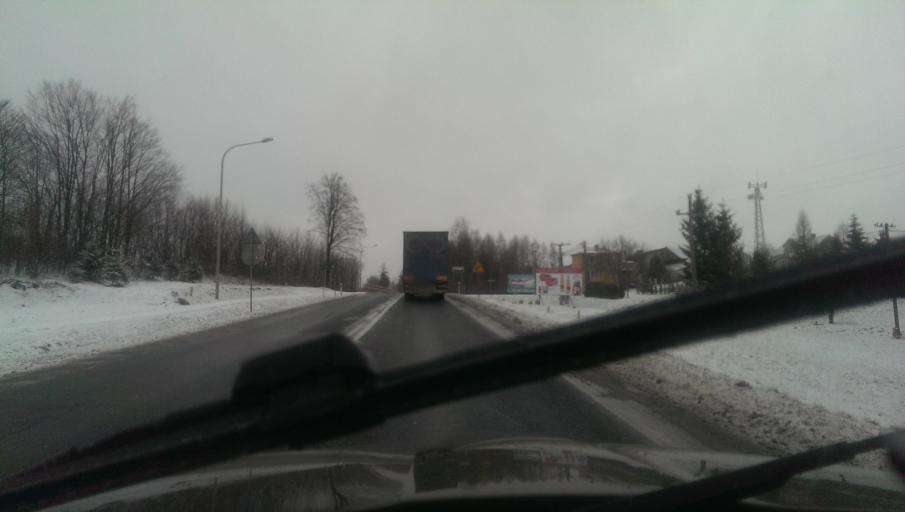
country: PL
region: Subcarpathian Voivodeship
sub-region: Powiat sanocki
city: Nowosielce-Gniewosz
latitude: 49.5732
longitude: 22.0602
